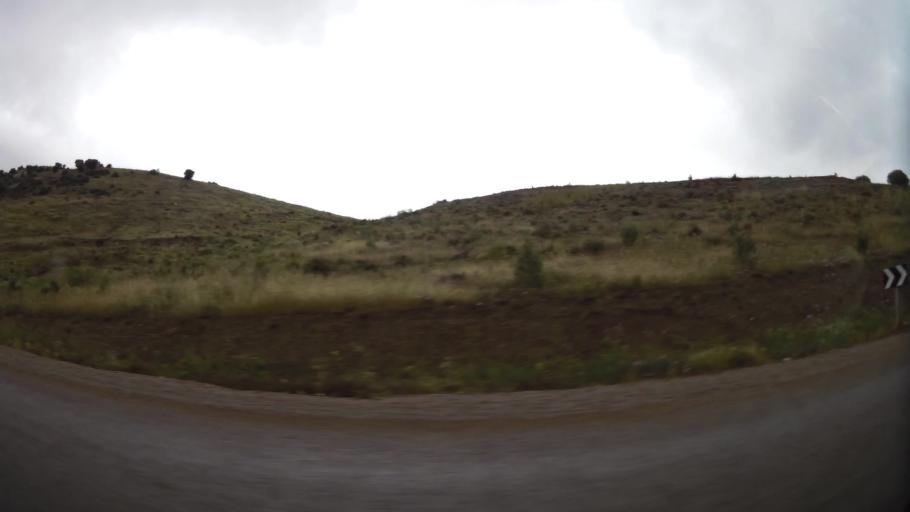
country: MA
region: Oriental
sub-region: Nador
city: Midar
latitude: 35.0690
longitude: -3.4810
